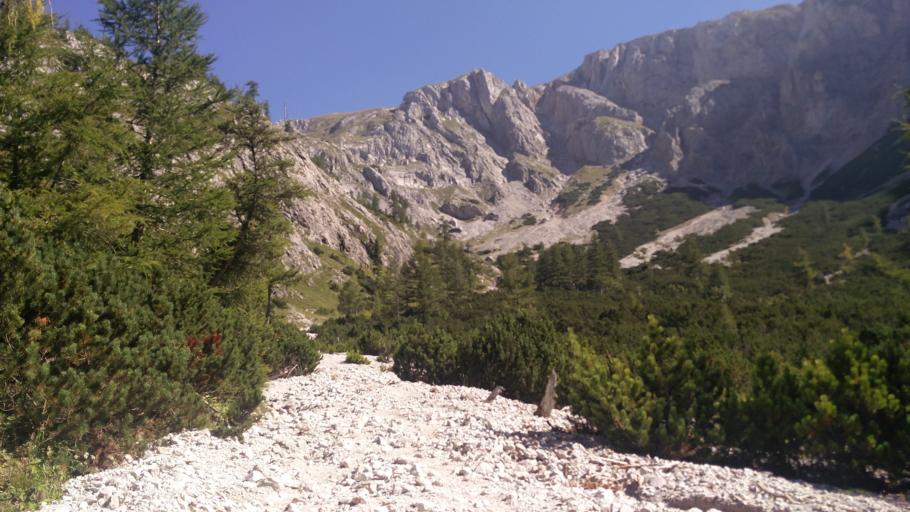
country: AT
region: Styria
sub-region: Politischer Bezirk Bruck-Muerzzuschlag
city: Sankt Ilgen
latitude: 47.6023
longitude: 15.1375
